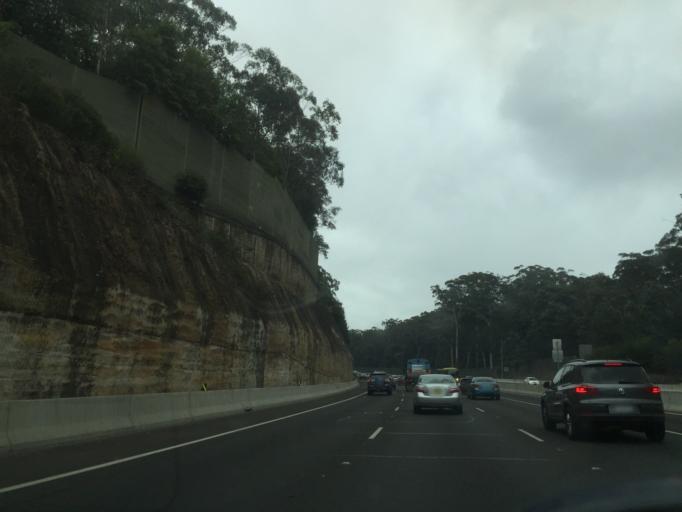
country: AU
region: New South Wales
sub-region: Hornsby Shire
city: Beecroft
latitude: -33.7578
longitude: 151.0639
